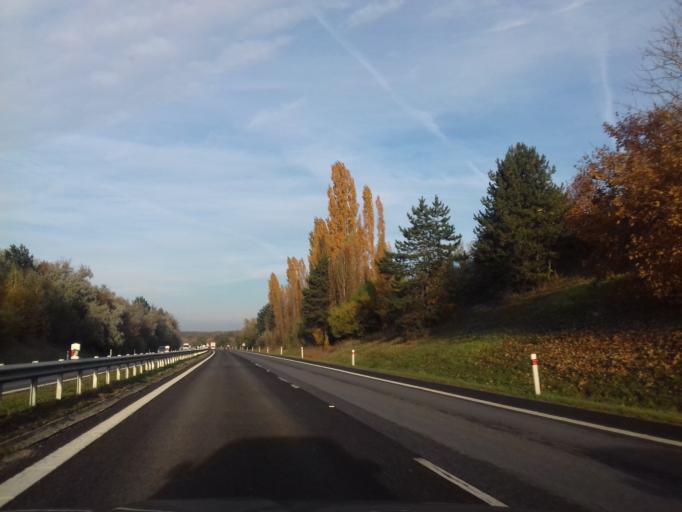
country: SK
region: Nitriansky
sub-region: Okres Nitra
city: Nitra
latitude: 48.3229
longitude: 17.9840
